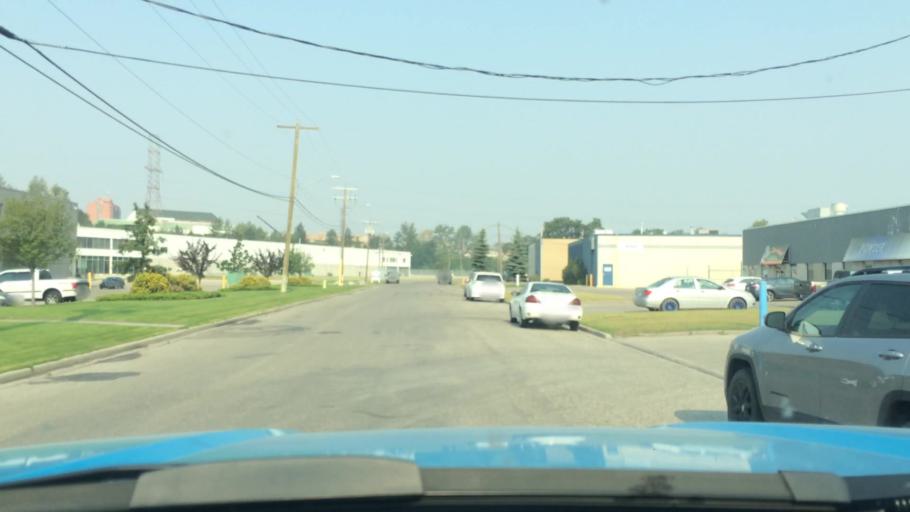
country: CA
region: Alberta
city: Calgary
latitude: 51.0111
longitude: -114.0548
